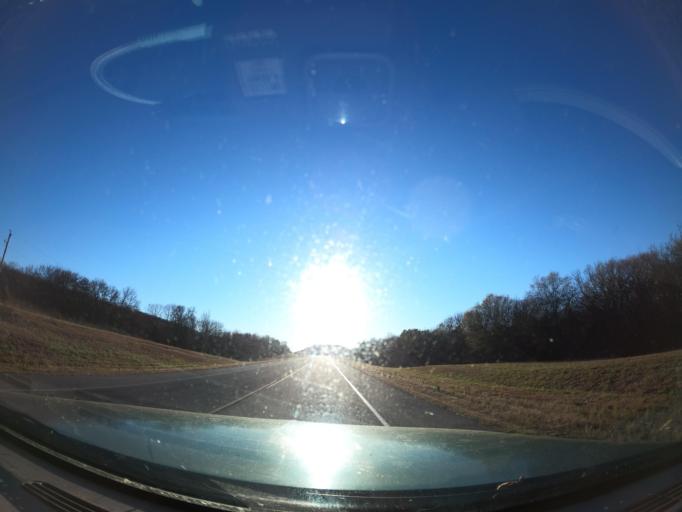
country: US
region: Oklahoma
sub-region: Pittsburg County
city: Hartshorne
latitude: 34.8659
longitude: -95.5233
